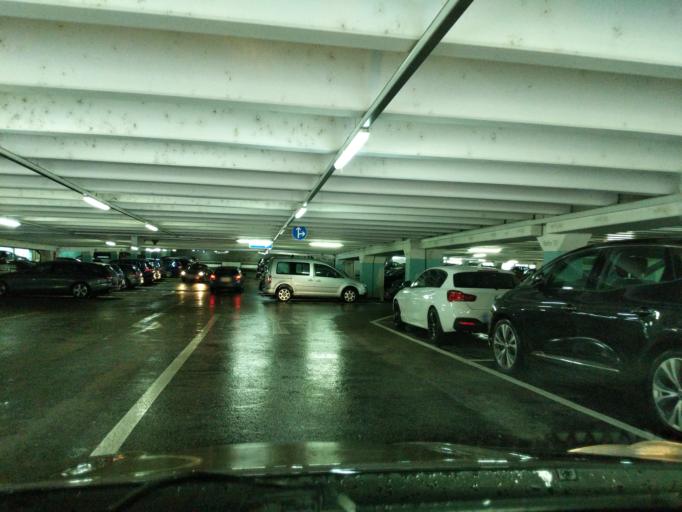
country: DE
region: Bavaria
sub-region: Upper Palatinate
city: Regensburg
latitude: 49.0244
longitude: 12.1160
